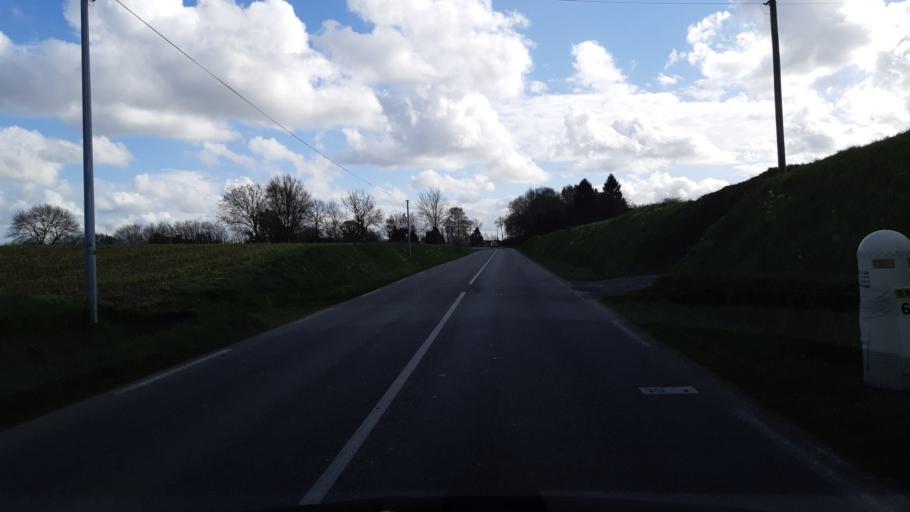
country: FR
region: Lower Normandy
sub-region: Departement de la Manche
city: Agneaux
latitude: 49.0604
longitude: -1.1331
